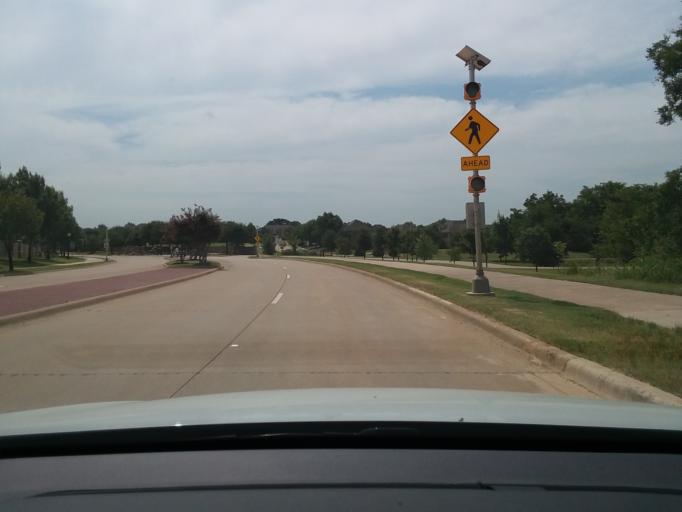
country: US
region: Texas
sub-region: Denton County
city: Flower Mound
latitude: 33.0308
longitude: -97.1046
